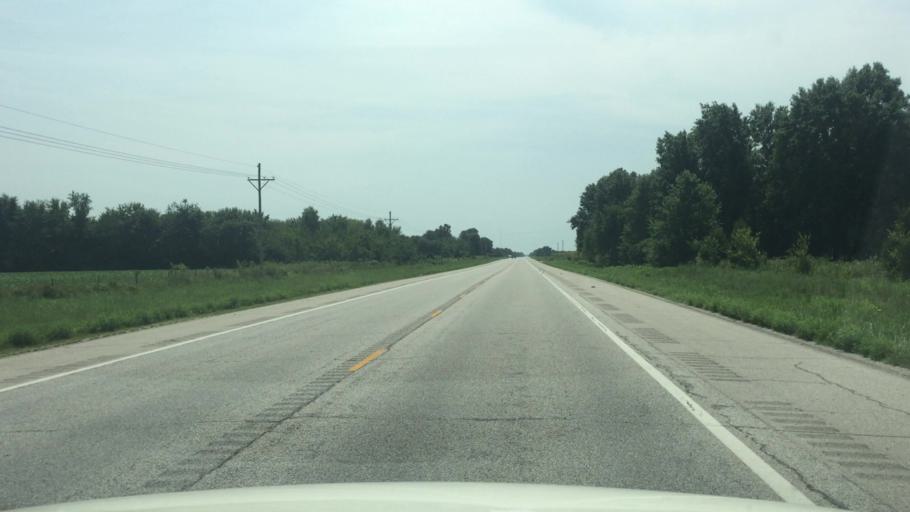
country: US
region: Kansas
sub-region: Cherokee County
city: Galena
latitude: 37.1546
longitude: -94.7043
